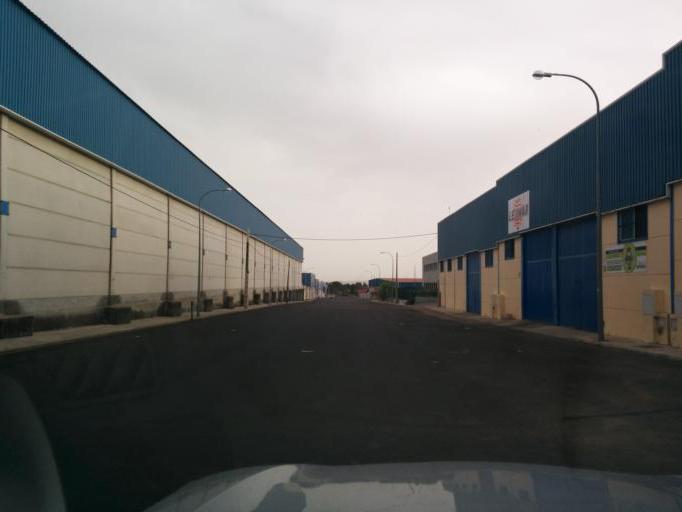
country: ES
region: Andalusia
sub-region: Provincia de Sevilla
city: Guillena
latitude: 37.5595
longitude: -6.0310
